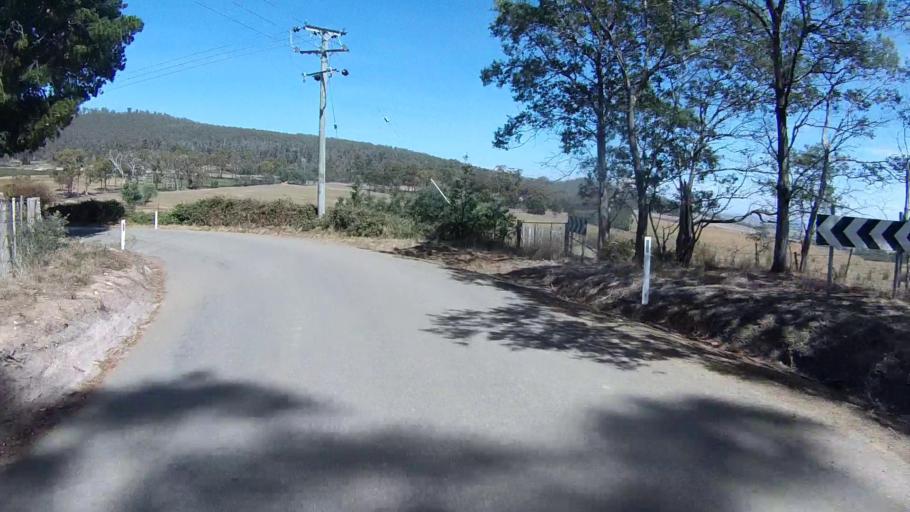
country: AU
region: Tasmania
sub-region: Sorell
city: Sorell
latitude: -42.7826
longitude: 147.6394
